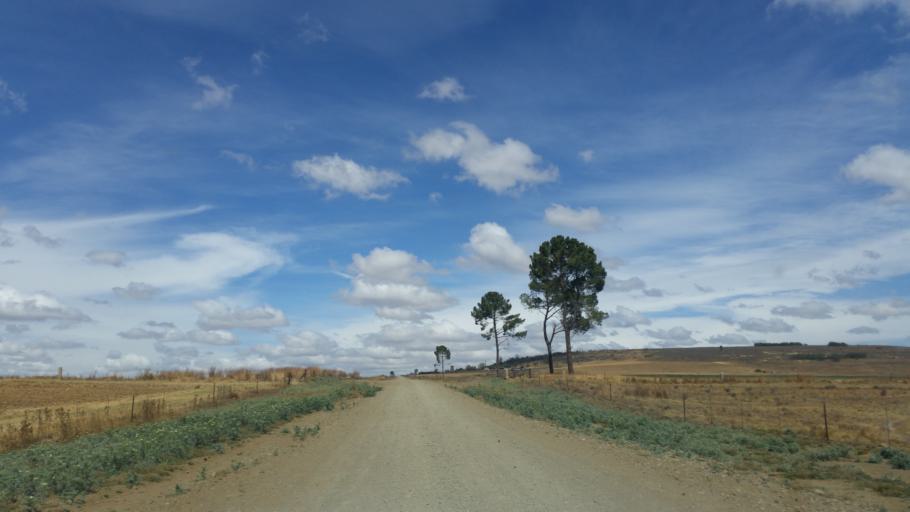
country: ZA
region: Orange Free State
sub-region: Thabo Mofutsanyana District Municipality
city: Bethlehem
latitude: -28.2414
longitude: 28.5779
